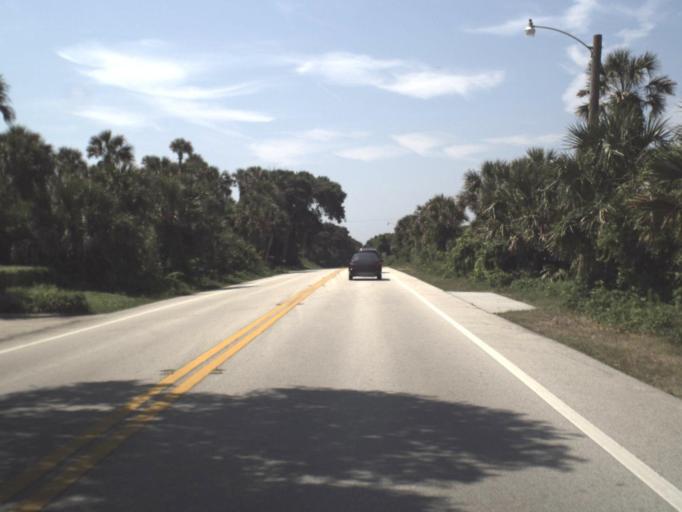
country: US
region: Florida
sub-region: Saint Johns County
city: Palm Valley
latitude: 30.1544
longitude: -81.3552
